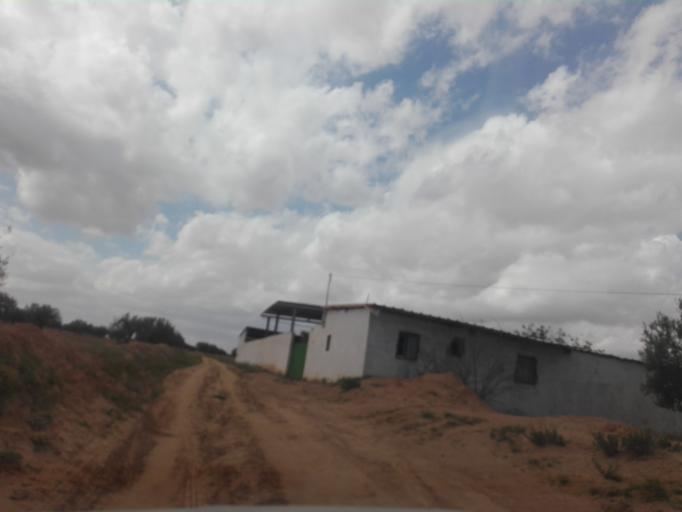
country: TN
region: Safaqis
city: Sfax
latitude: 34.6913
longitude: 10.4509
